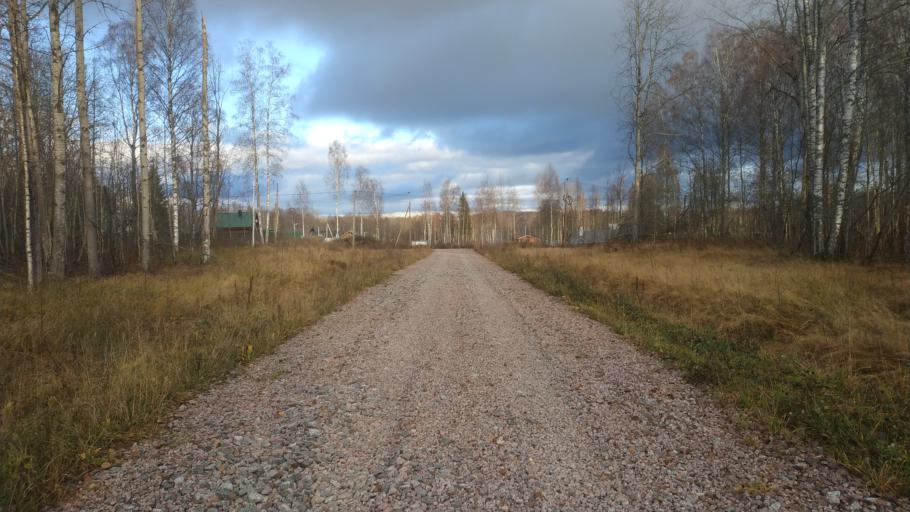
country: RU
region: Leningrad
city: Agalatovo
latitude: 60.3247
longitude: 30.2310
